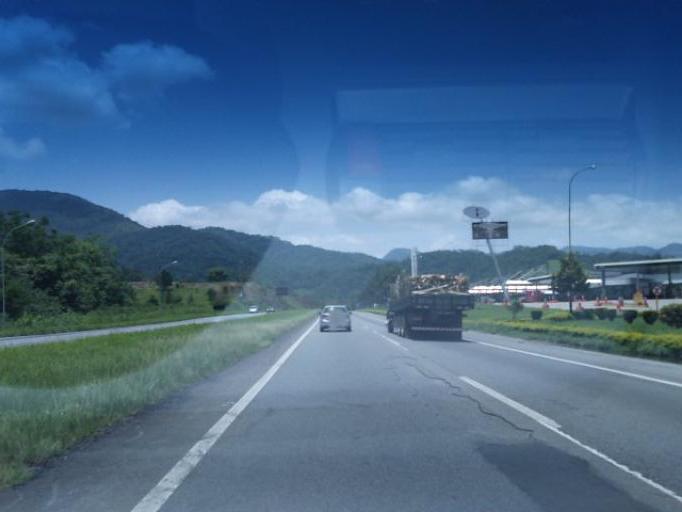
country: BR
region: Sao Paulo
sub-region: Miracatu
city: Miracatu
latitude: -24.2571
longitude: -47.3763
